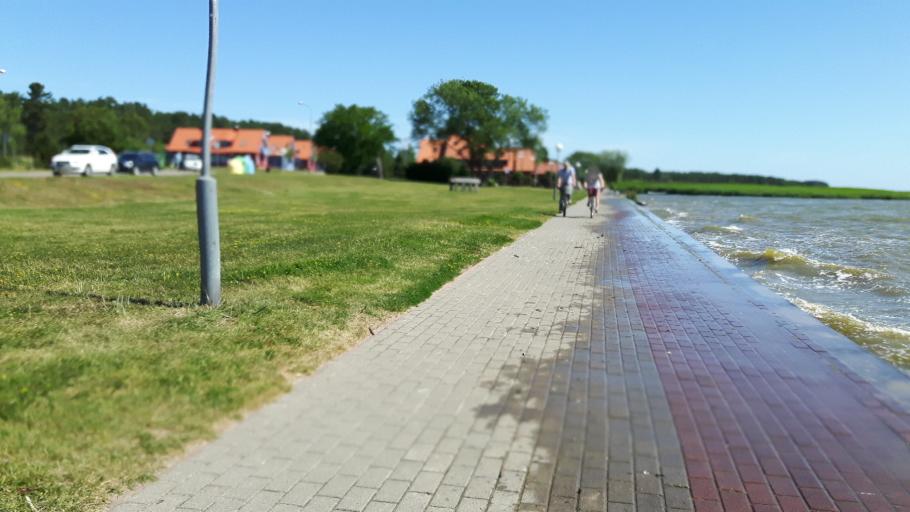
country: LT
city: Nida
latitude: 55.3159
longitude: 21.0183
